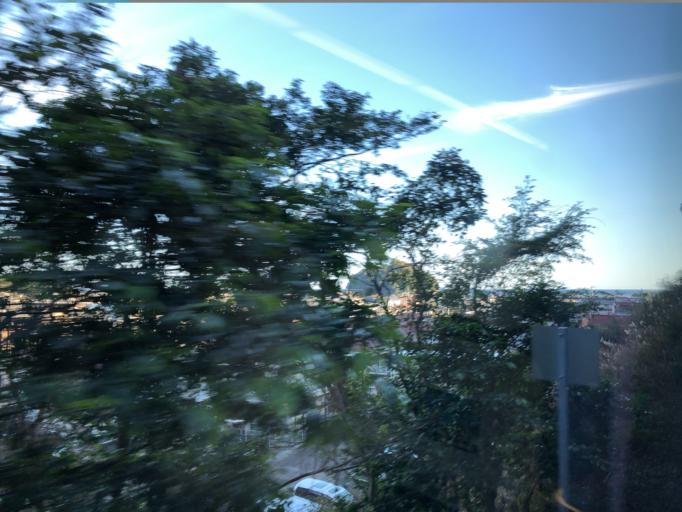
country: JP
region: Kochi
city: Nakamura
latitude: 33.0769
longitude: 133.1035
